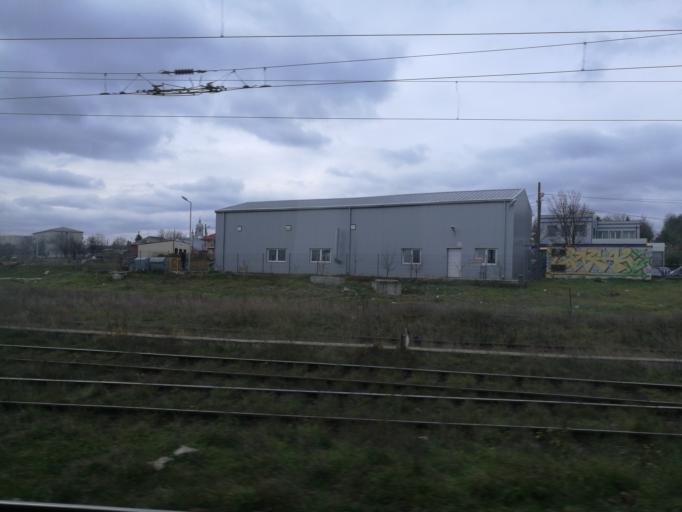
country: RO
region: Iasi
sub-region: Municipiul Pascani
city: Pascani
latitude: 47.2439
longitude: 26.7321
